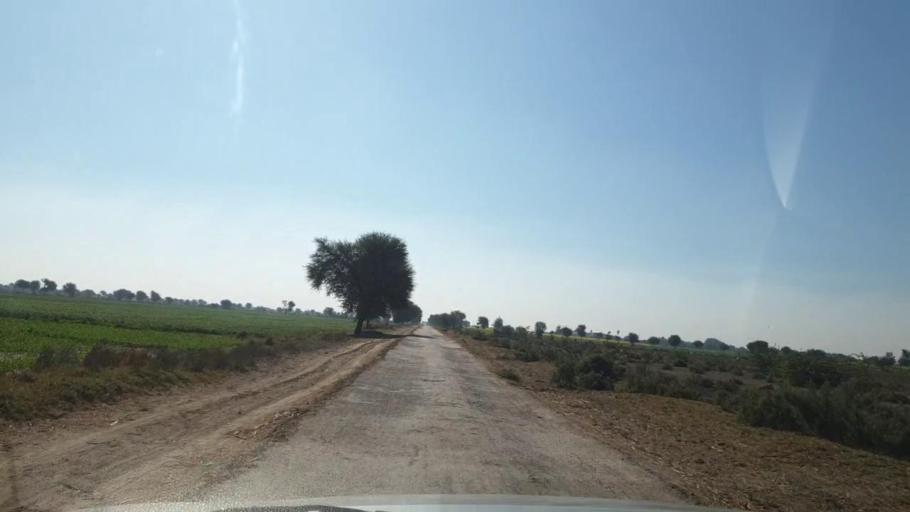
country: PK
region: Sindh
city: Jhol
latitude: 25.8183
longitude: 69.0358
